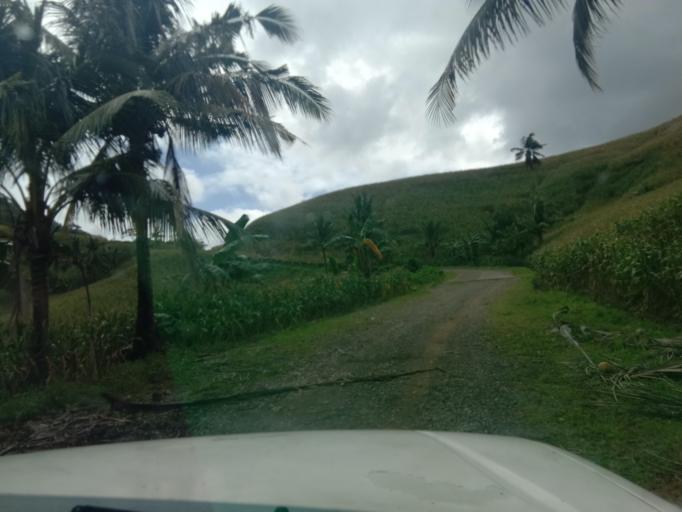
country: PH
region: Western Visayas
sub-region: Province of Capiz
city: Lantangan
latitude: 11.3551
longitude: 122.9162
